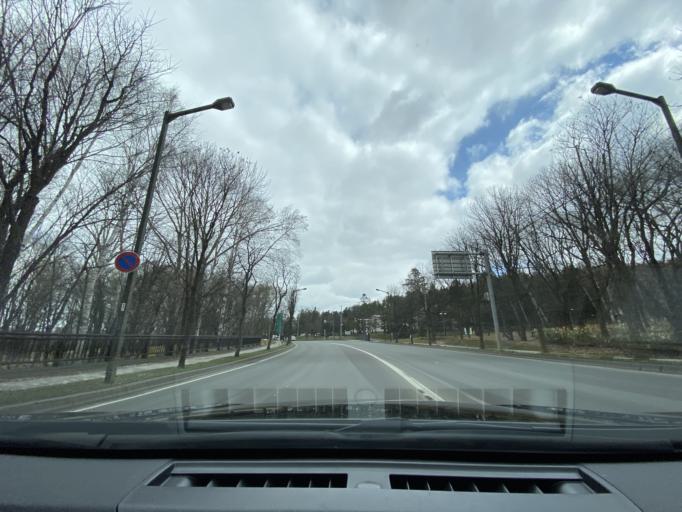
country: JP
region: Hokkaido
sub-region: Asahikawa-shi
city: Asahikawa
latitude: 43.7510
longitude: 142.3615
